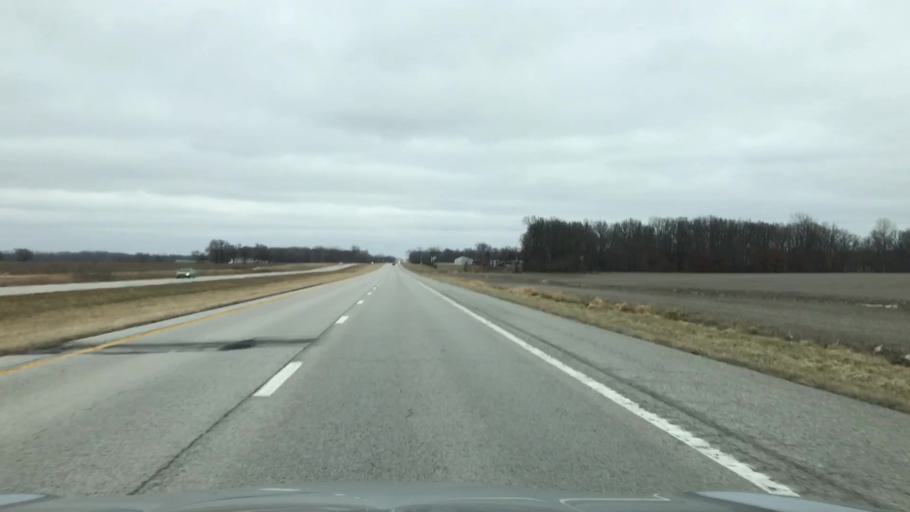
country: US
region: Missouri
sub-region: Livingston County
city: Chillicothe
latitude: 39.7765
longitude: -93.4519
